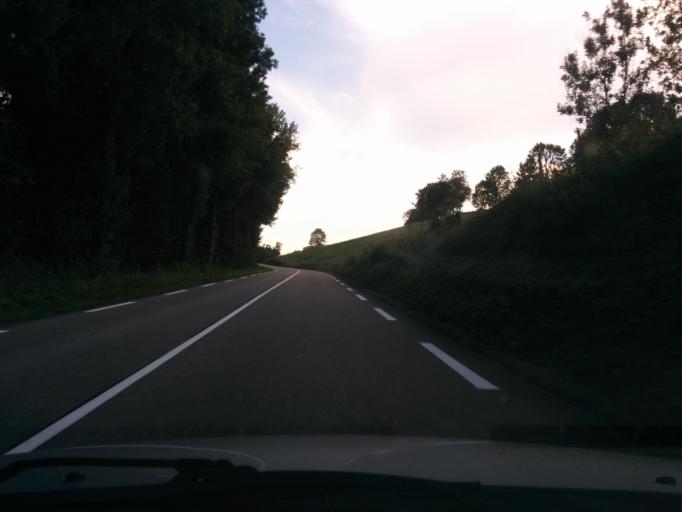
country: FR
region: Rhone-Alpes
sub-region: Departement de l'Isere
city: La Buisse
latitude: 45.3356
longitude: 5.6596
